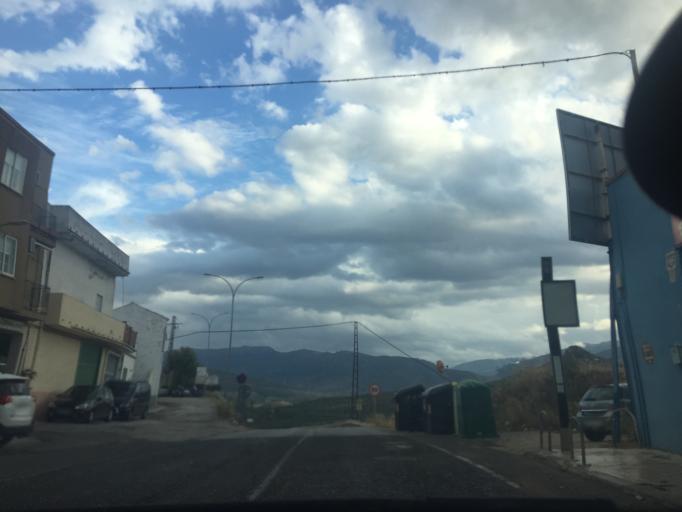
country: ES
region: Andalusia
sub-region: Provincia de Jaen
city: Jaen
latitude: 37.7667
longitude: -3.7745
